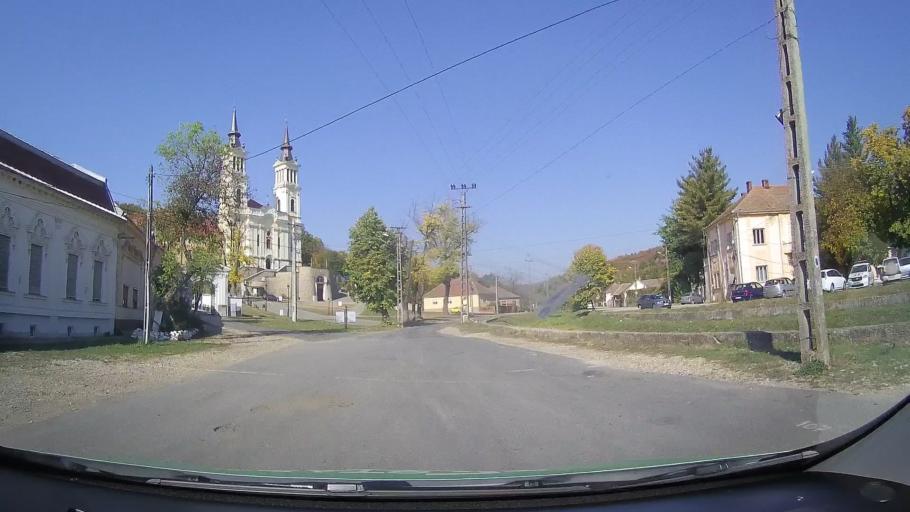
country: RO
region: Arad
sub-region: Oras Lipova
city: Radna
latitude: 46.0980
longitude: 21.6876
